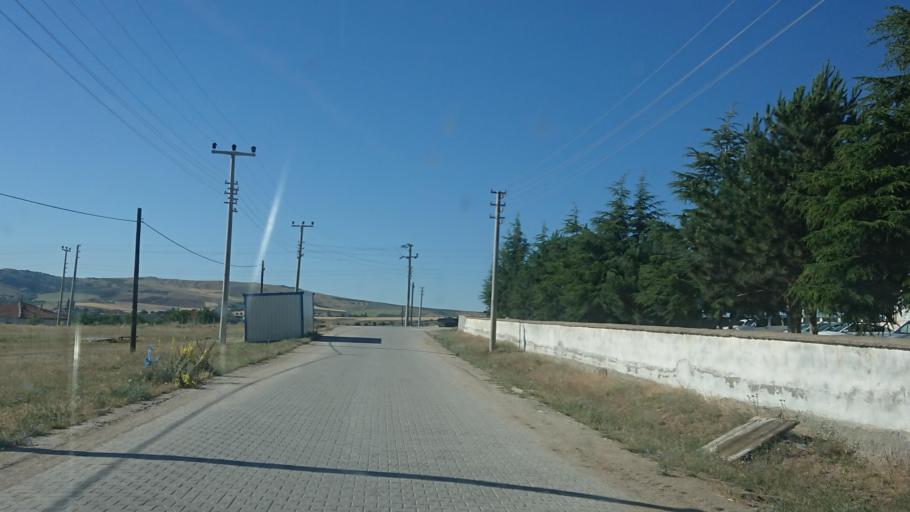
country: TR
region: Aksaray
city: Agacoren
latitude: 38.8702
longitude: 33.9454
